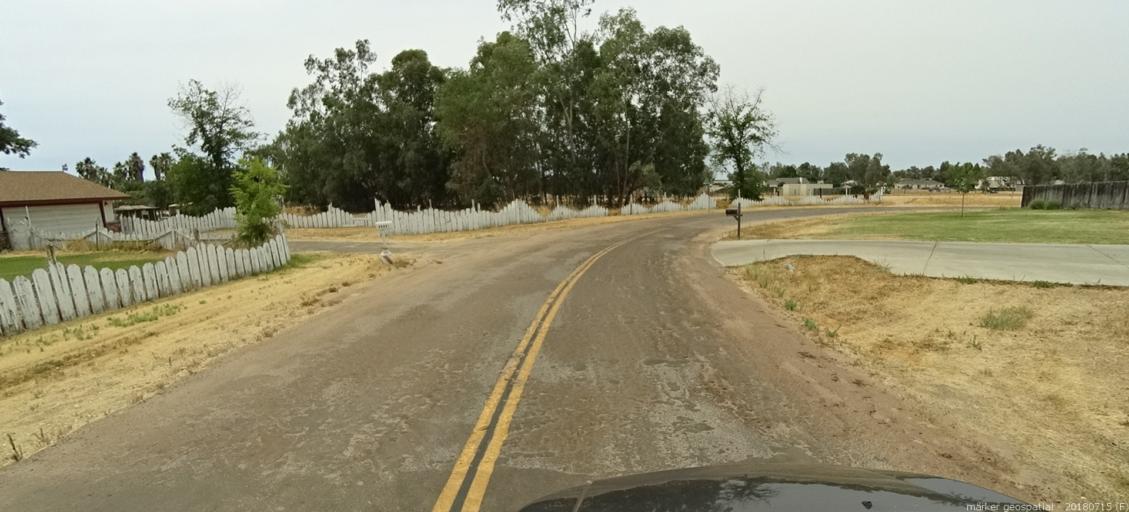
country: US
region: California
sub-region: Madera County
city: Madera Acres
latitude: 37.0109
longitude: -120.0861
